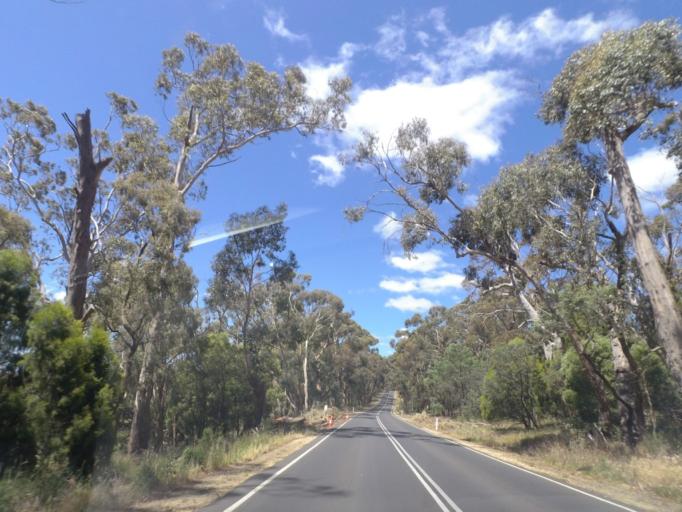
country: AU
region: Victoria
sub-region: Mount Alexander
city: Castlemaine
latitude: -37.2882
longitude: 144.2731
